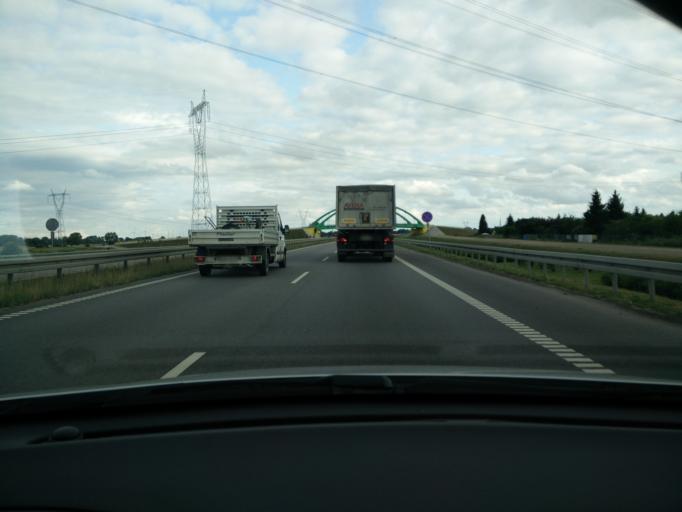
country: PL
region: Pomeranian Voivodeship
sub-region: Gdansk
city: Gdansk
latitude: 54.3353
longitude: 18.7024
